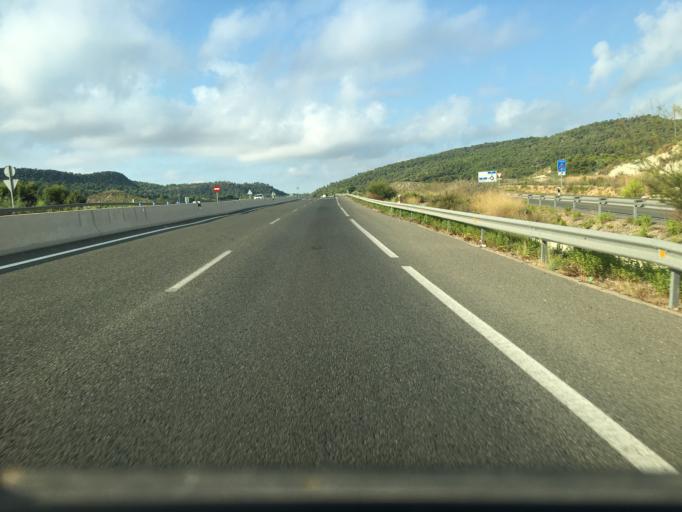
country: ES
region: Murcia
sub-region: Murcia
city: Beniel
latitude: 37.9396
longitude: -0.9537
